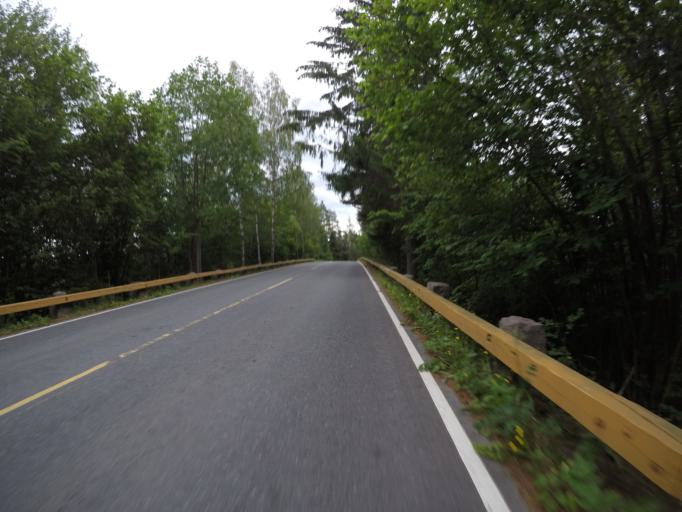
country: FI
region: Haeme
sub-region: Haemeenlinna
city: Haemeenlinna
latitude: 60.9731
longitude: 24.4694
